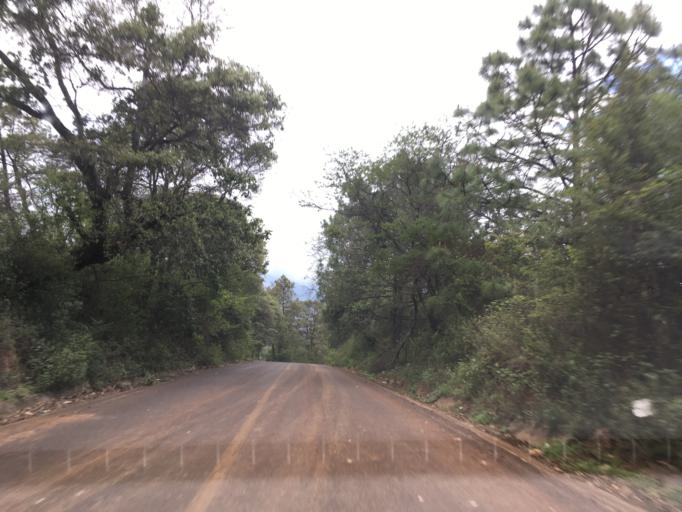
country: MX
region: Michoacan
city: Acuitzio del Canje
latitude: 19.5367
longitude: -101.2581
